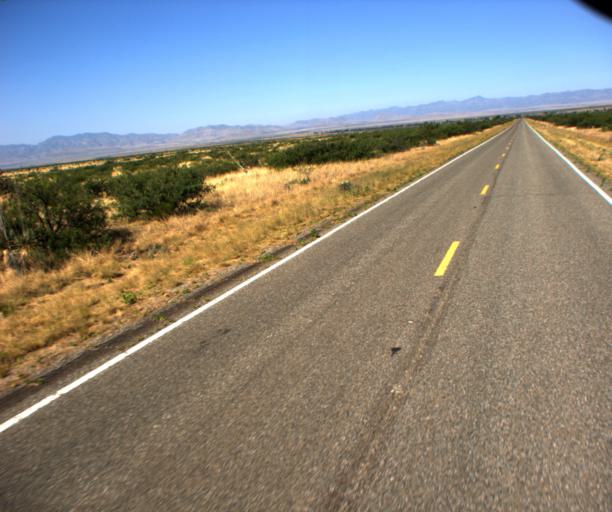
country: US
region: Arizona
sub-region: Graham County
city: Swift Trail Junction
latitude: 32.5856
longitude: -109.9293
